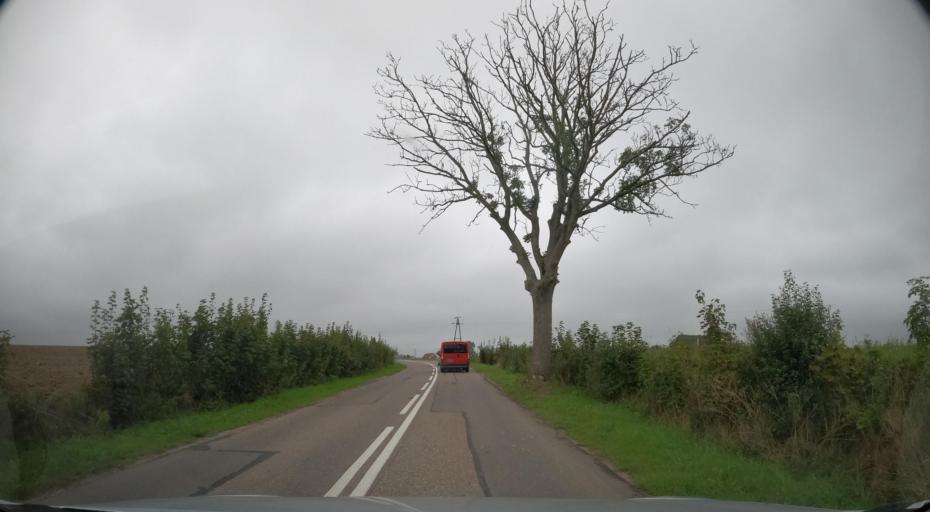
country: PL
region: Pomeranian Voivodeship
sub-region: Powiat wejherowski
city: Luzino
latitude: 54.4967
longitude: 18.1418
